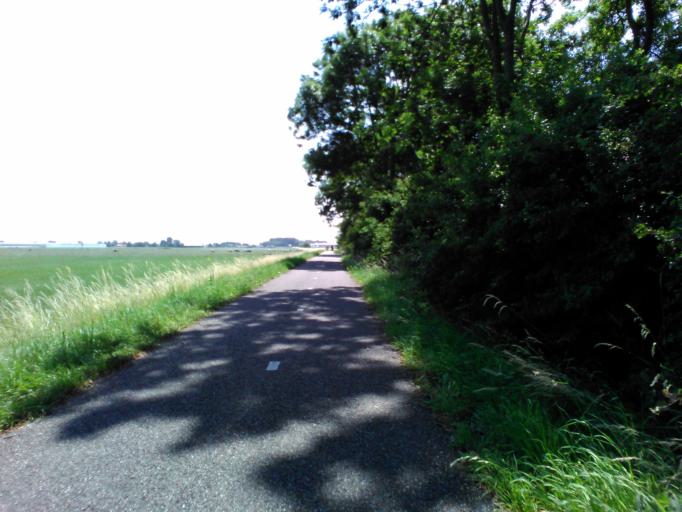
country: NL
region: South Holland
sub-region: Gemeente Westland
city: De Lier
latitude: 51.9586
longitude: 4.2651
